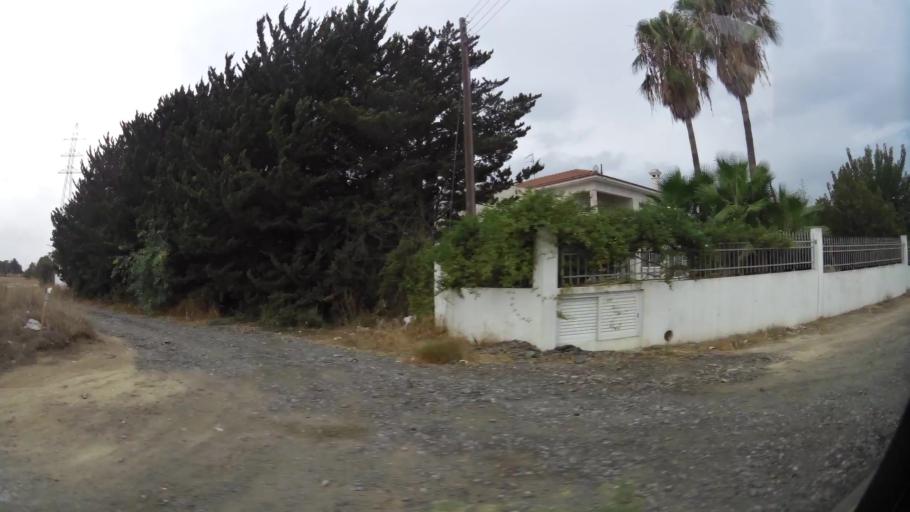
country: CY
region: Lefkosia
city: Geri
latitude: 35.0959
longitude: 33.3895
